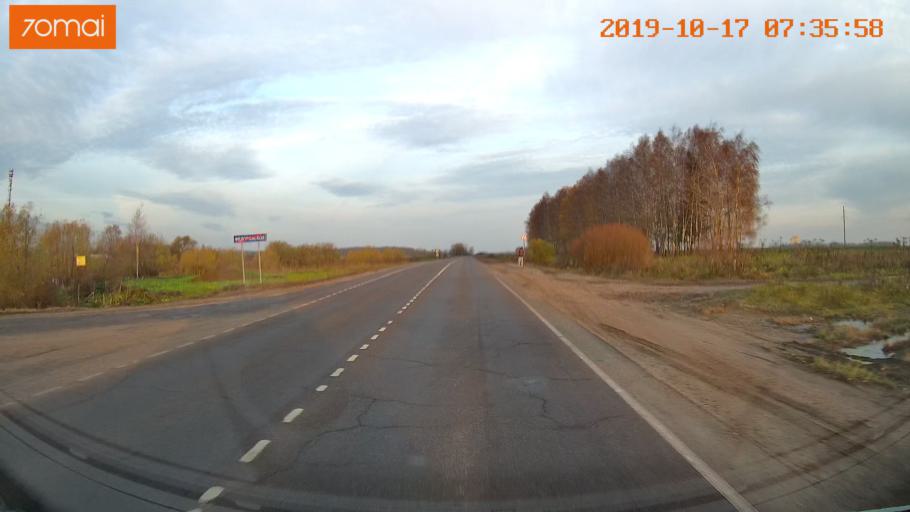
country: RU
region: Ivanovo
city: Gavrilov Posad
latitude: 56.4335
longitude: 39.9221
